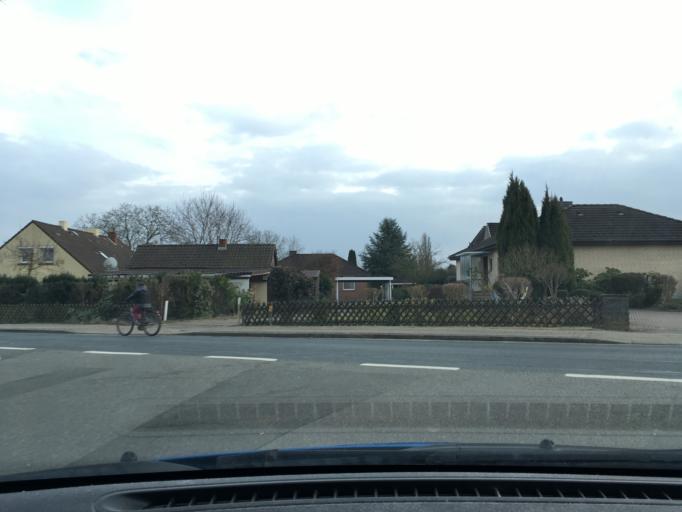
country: DE
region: Lower Saxony
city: Reppenstedt
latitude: 53.2503
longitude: 10.3485
